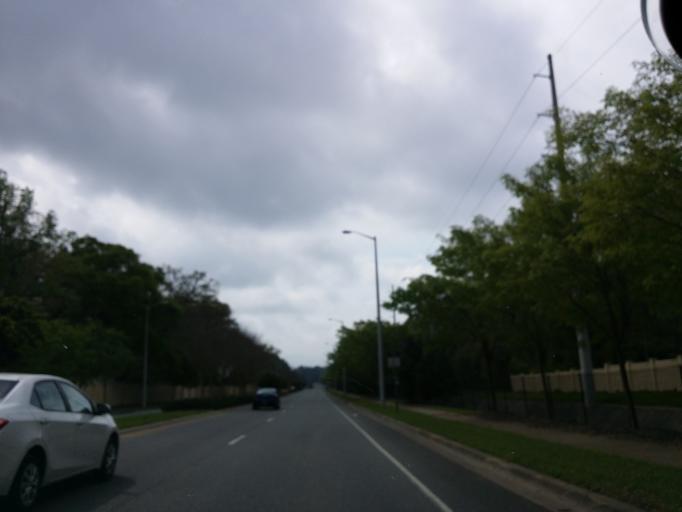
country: US
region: Florida
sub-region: Leon County
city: Tallahassee
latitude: 30.4718
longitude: -84.2439
